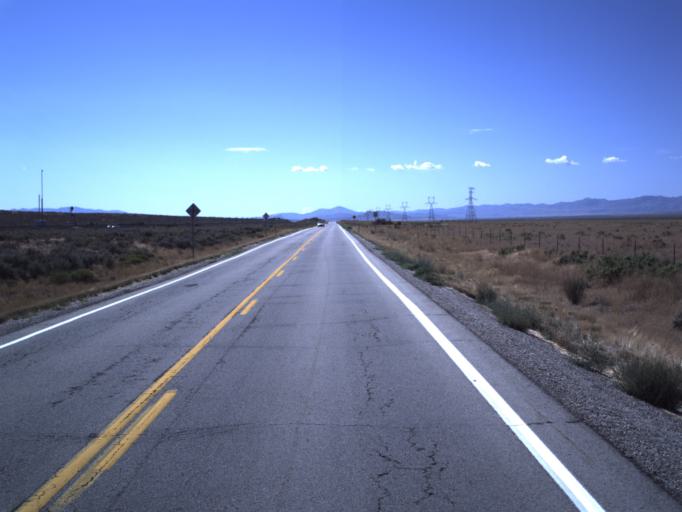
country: US
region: Utah
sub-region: Tooele County
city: Tooele
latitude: 40.3627
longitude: -112.4145
